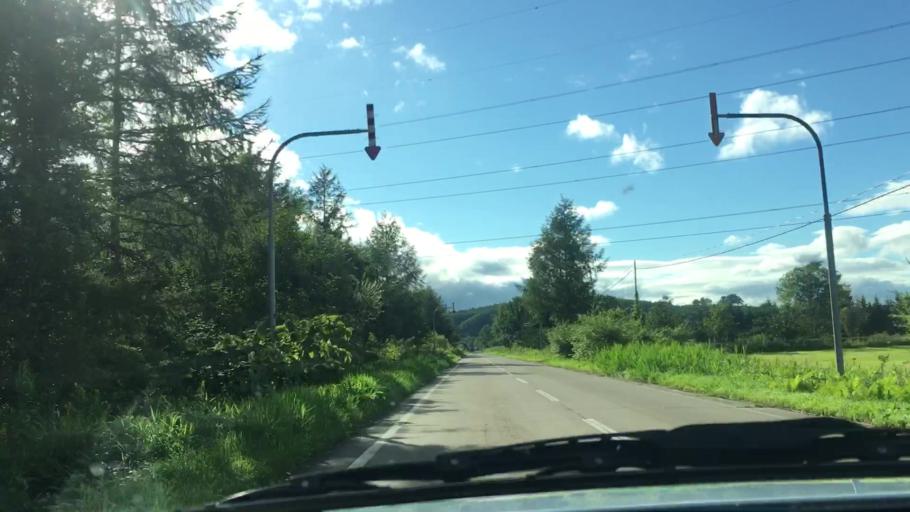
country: JP
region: Hokkaido
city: Otofuke
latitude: 43.1700
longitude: 143.0012
